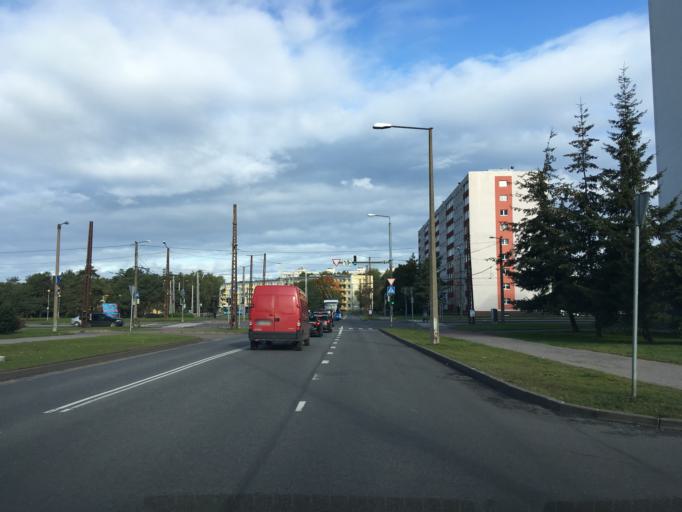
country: EE
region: Harju
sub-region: Tallinna linn
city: Tallinn
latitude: 59.3981
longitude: 24.6815
